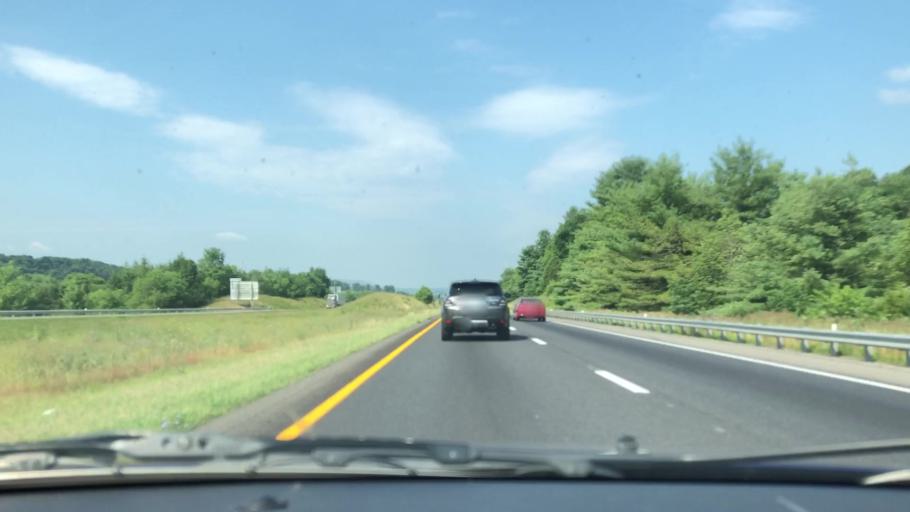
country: US
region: Virginia
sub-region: Montgomery County
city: Christiansburg
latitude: 37.1127
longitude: -80.4431
